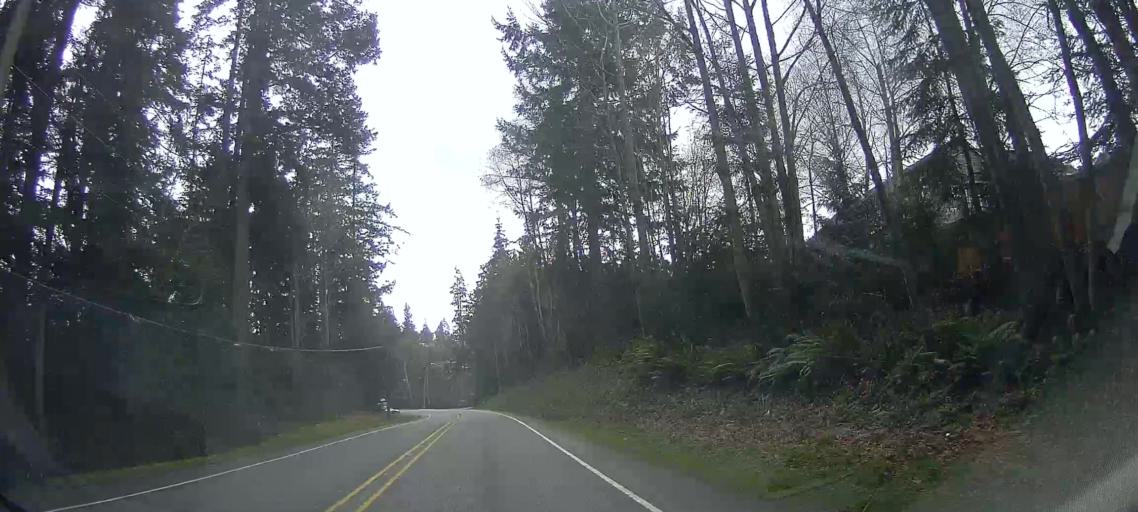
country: US
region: Washington
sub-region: Island County
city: Camano
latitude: 48.1688
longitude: -122.4815
